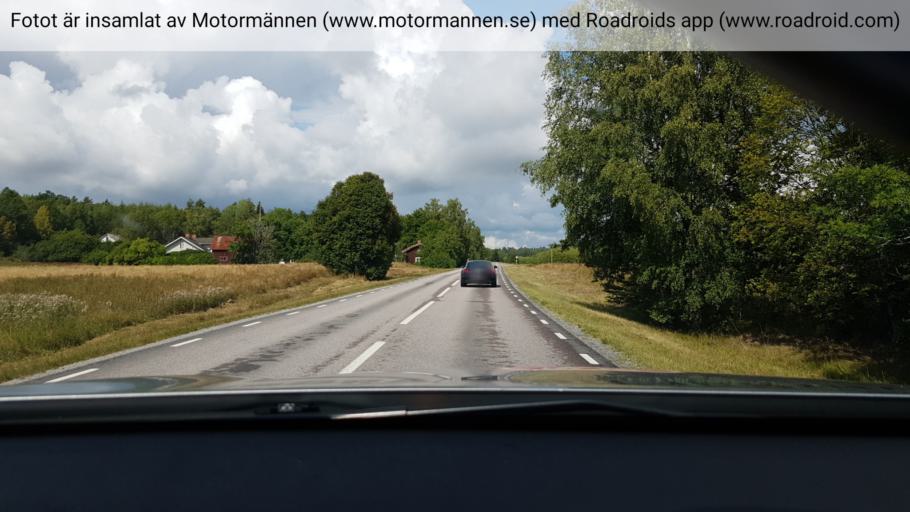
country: SE
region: Stockholm
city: Stenhamra
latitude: 59.3510
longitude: 17.6239
